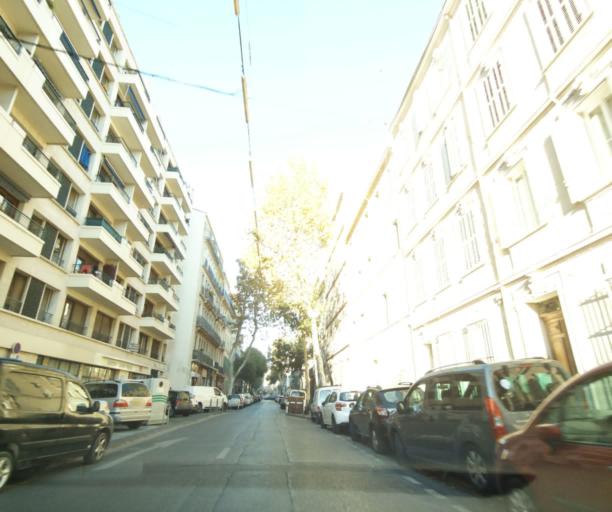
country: FR
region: Provence-Alpes-Cote d'Azur
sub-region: Departement des Bouches-du-Rhone
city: Marseille 04
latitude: 43.3036
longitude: 5.3977
